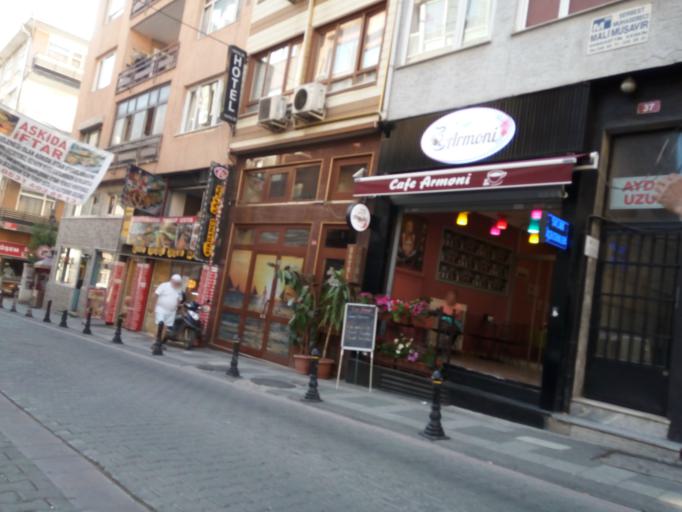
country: TR
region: Istanbul
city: UEskuedar
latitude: 40.9933
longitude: 29.0272
